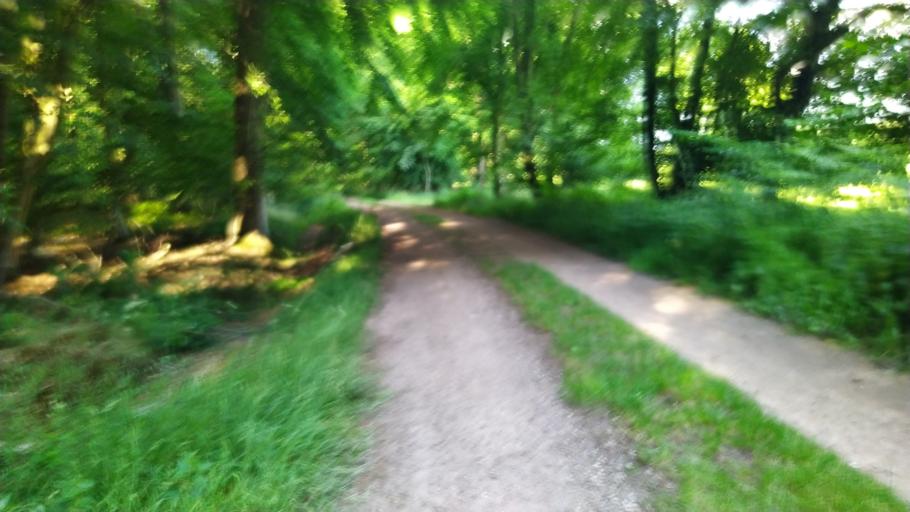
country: DE
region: Lower Saxony
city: Lintig
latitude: 53.5944
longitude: 8.8996
